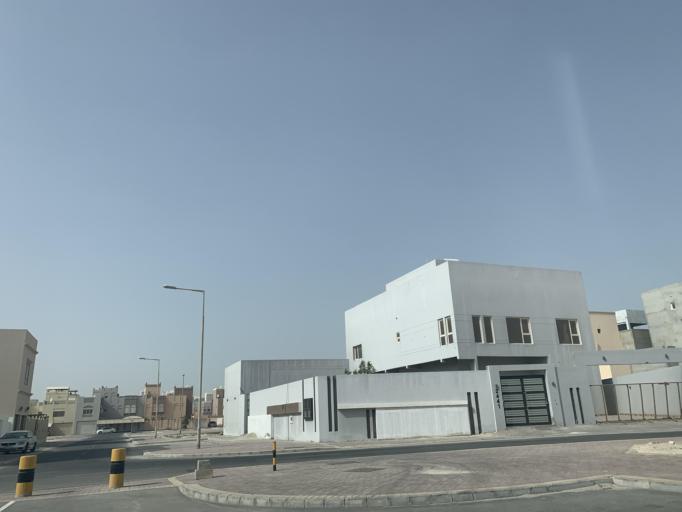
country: BH
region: Northern
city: Madinat `Isa
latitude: 26.1638
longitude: 50.5368
